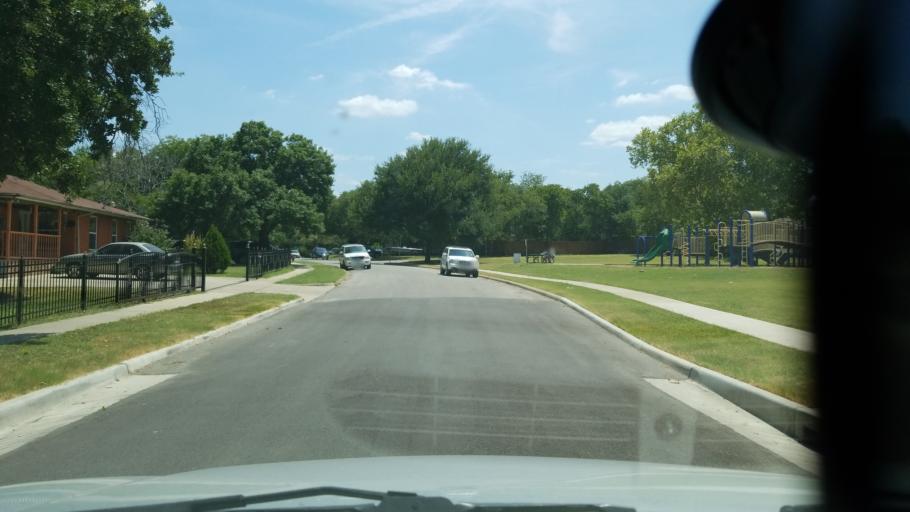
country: US
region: Texas
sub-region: Dallas County
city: Grand Prairie
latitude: 32.7568
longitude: -96.9770
